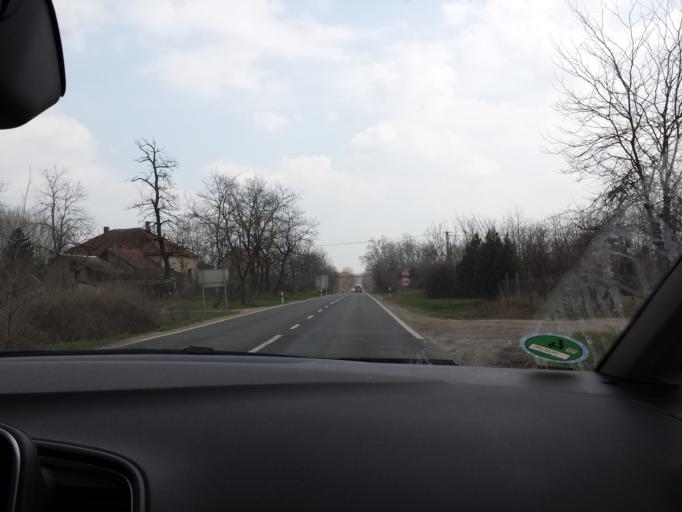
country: HU
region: Bacs-Kiskun
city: Lakitelek
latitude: 46.8775
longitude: 20.0194
